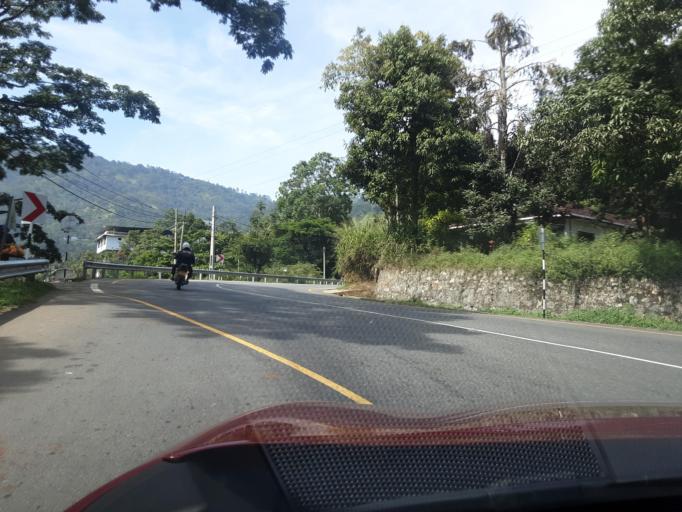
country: LK
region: Uva
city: Badulla
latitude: 6.9755
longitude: 81.0855
